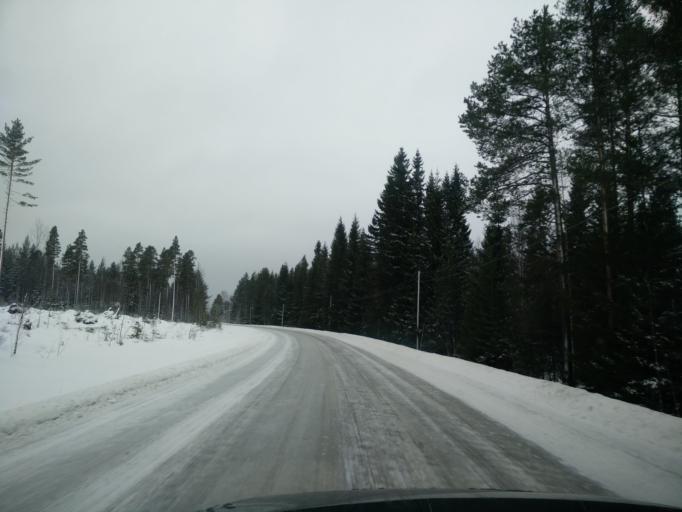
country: SE
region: Jaemtland
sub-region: Braecke Kommun
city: Braecke
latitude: 62.4044
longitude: 15.3065
